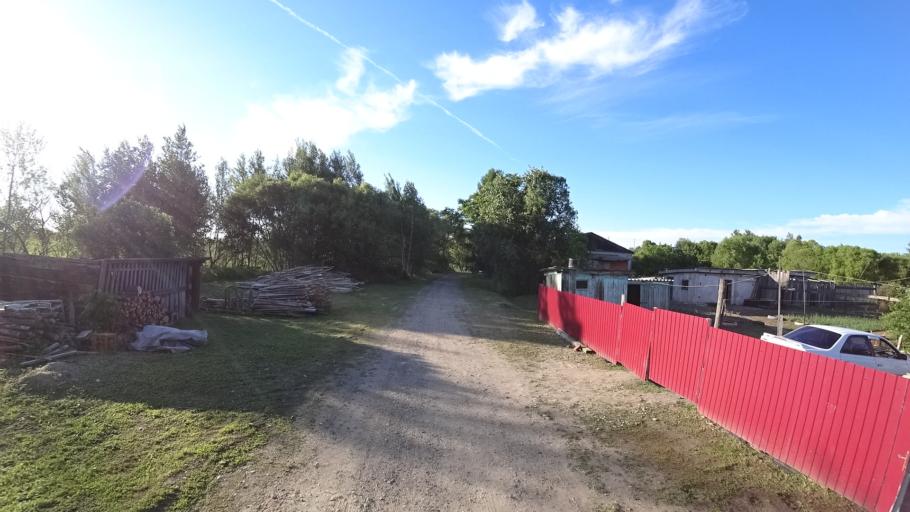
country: RU
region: Khabarovsk Krai
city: Khor
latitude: 47.8511
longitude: 134.9424
